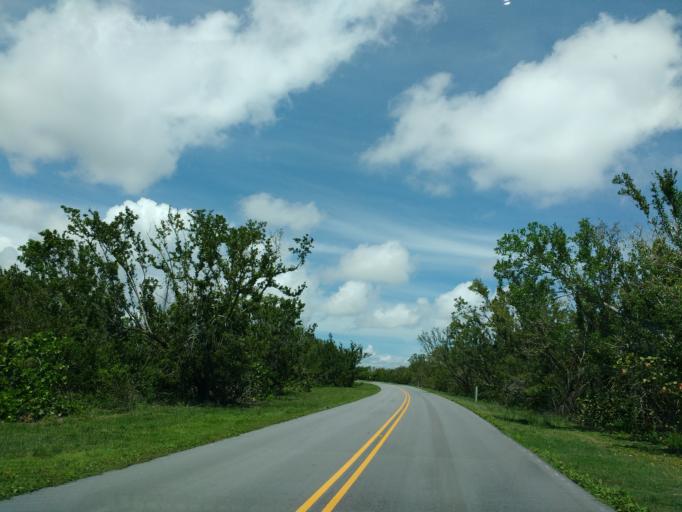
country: US
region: Florida
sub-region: Monroe County
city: Islamorada
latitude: 25.1391
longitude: -80.9314
